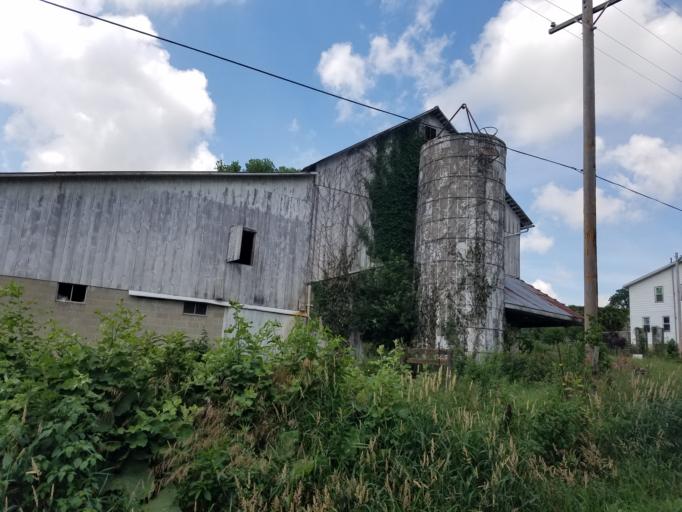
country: US
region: Ohio
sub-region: Knox County
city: Danville
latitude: 40.5545
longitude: -82.3467
